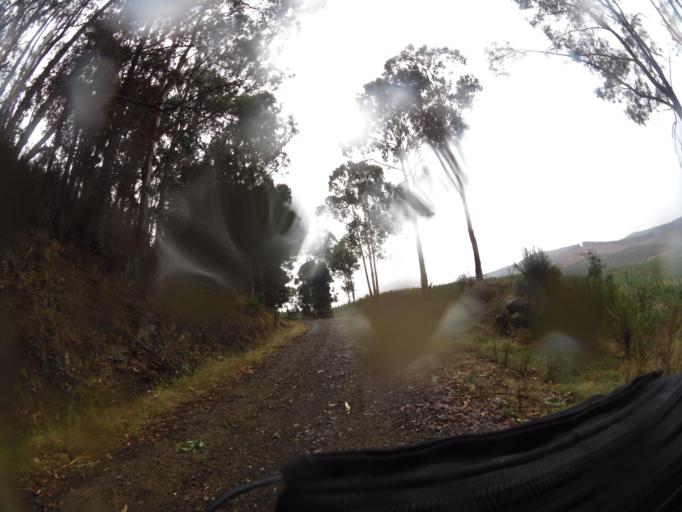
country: AU
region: New South Wales
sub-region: Greater Hume Shire
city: Holbrook
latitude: -36.2189
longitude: 147.5659
